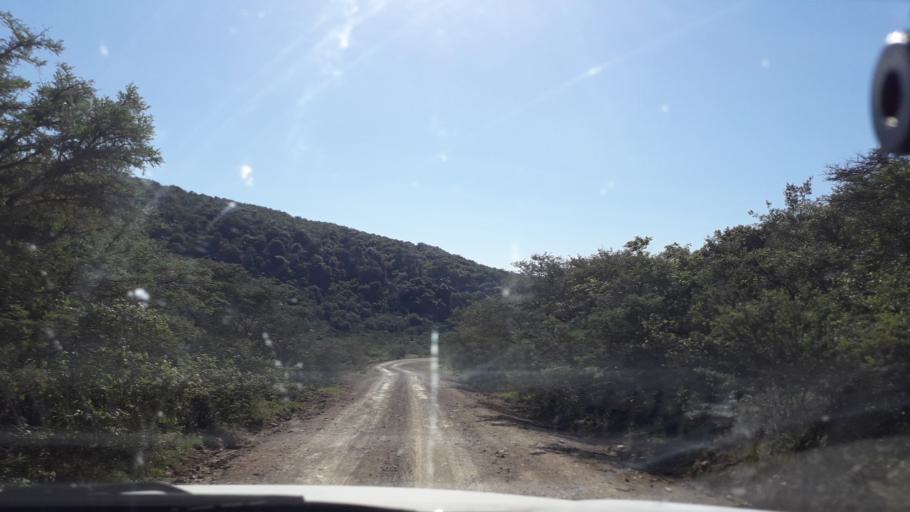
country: ZA
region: Eastern Cape
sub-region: Amathole District Municipality
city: Komga
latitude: -32.7714
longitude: 27.9605
